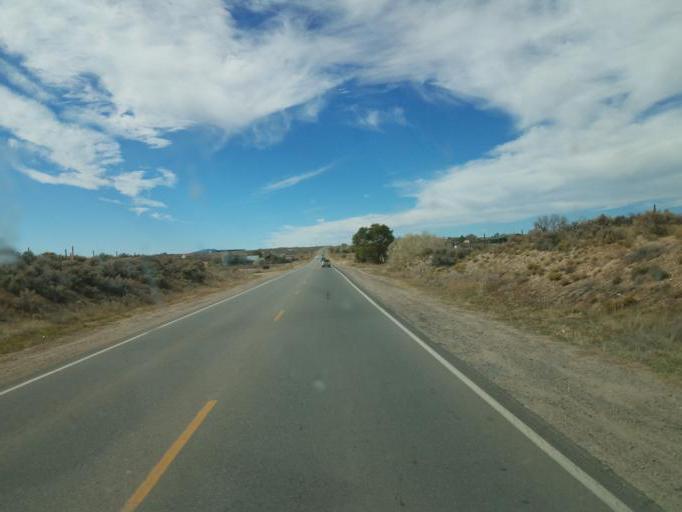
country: US
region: New Mexico
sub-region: Taos County
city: Taos
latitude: 36.4570
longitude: -105.6042
